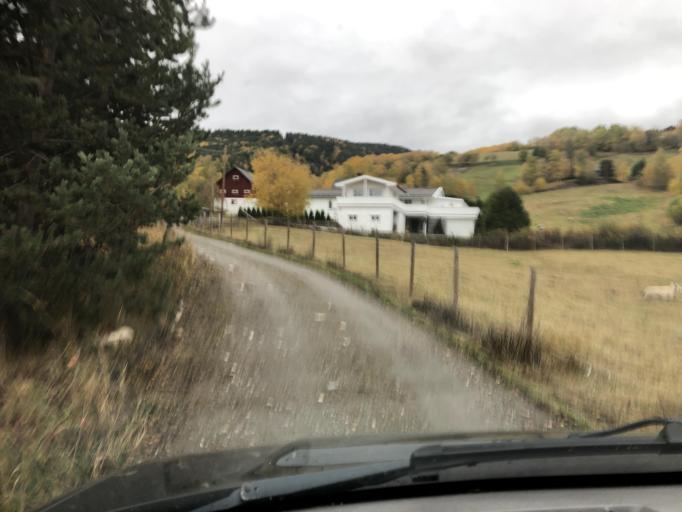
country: NO
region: Oppland
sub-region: Sor-Fron
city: Hundorp
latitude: 61.5741
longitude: 9.9141
